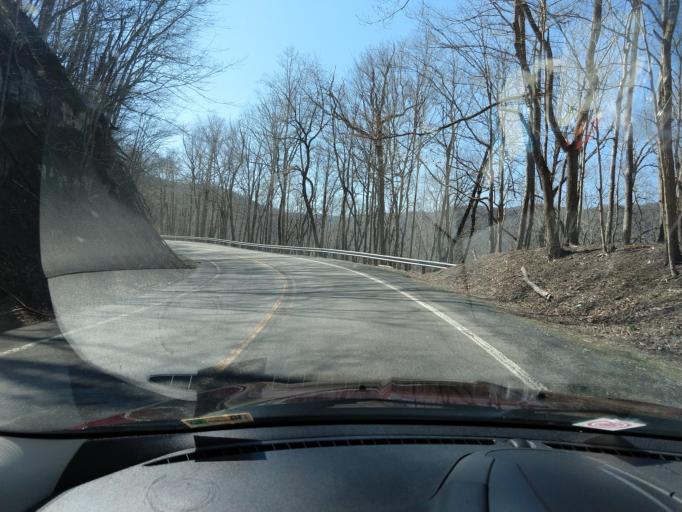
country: US
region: West Virginia
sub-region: Summers County
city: Hinton
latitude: 37.7489
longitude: -80.9121
